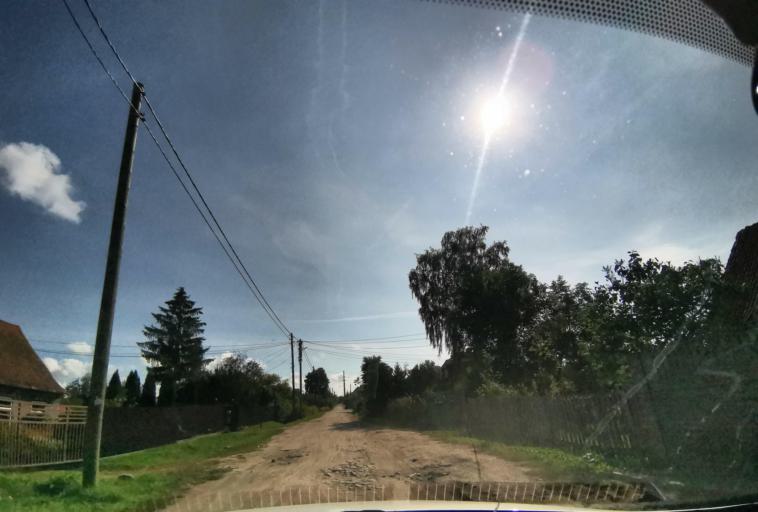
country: RU
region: Kaliningrad
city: Chernyakhovsk
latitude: 54.6578
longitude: 21.8410
